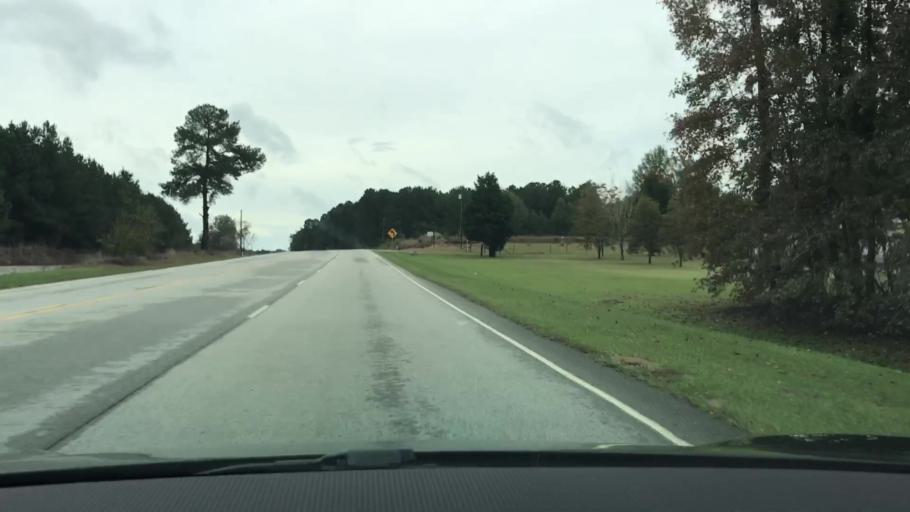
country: US
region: Georgia
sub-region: Warren County
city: Firing Range
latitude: 33.4881
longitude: -82.7964
